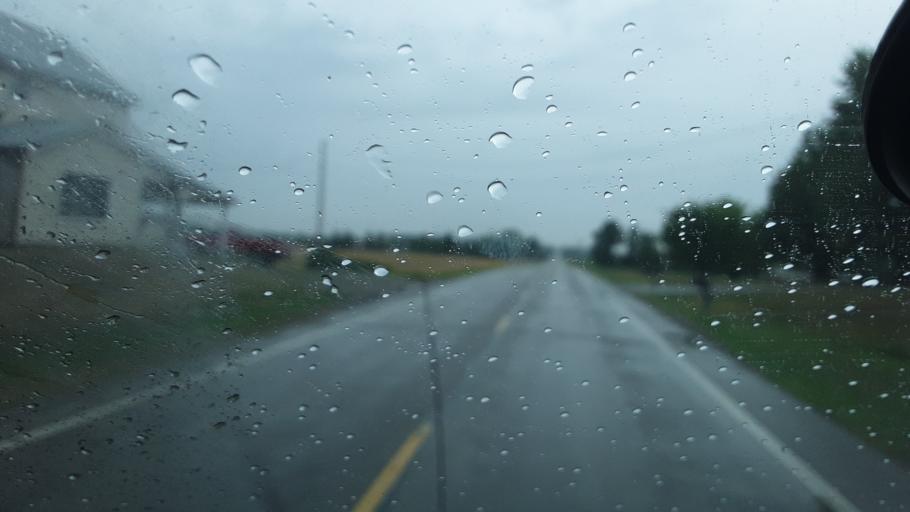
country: US
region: Ohio
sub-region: Williams County
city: Montpelier
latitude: 41.5436
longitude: -84.6130
